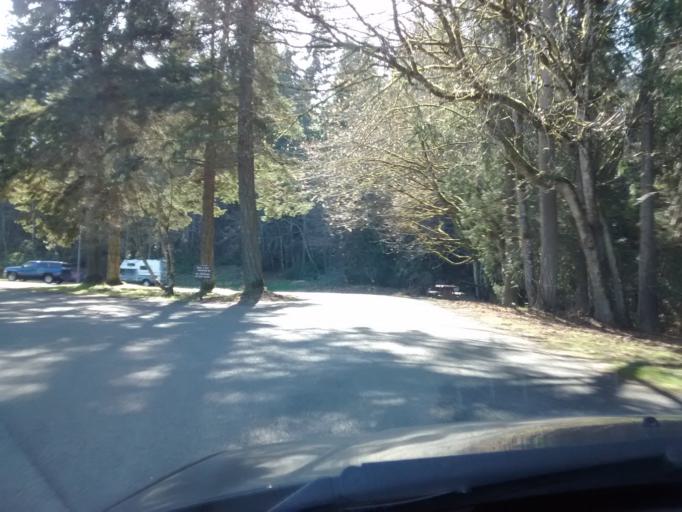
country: US
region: Washington
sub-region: Clallam County
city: Port Angeles
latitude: 48.1001
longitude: -123.4264
